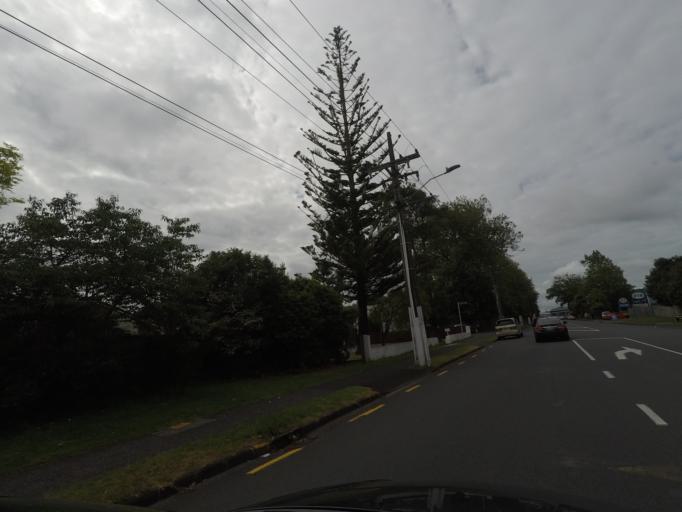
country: NZ
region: Auckland
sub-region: Auckland
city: Rosebank
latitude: -36.8653
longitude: 174.6155
